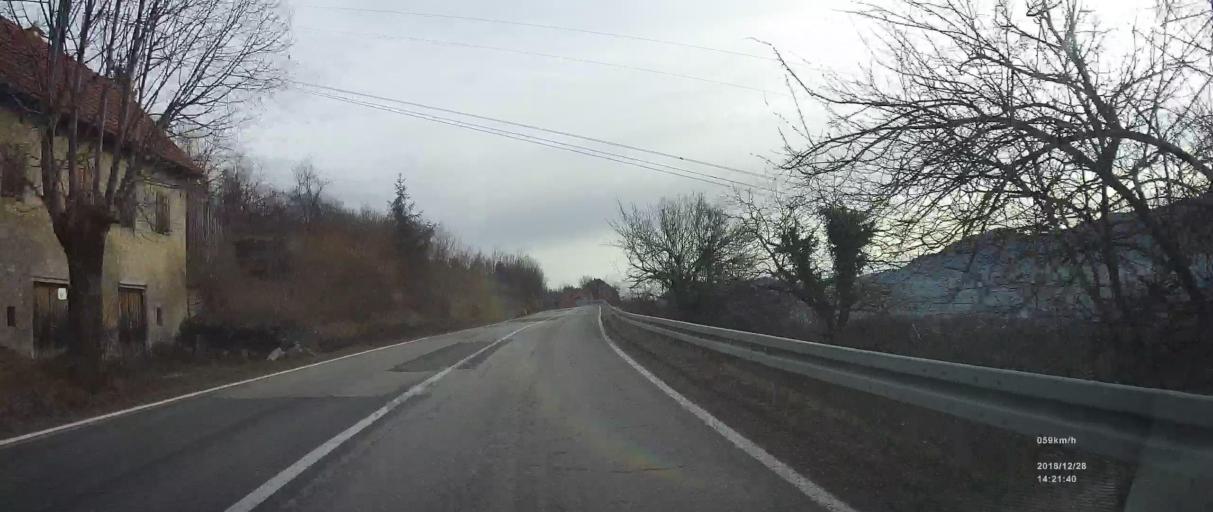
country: HR
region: Primorsko-Goranska
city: Vrbovsko
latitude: 45.3918
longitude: 15.0826
